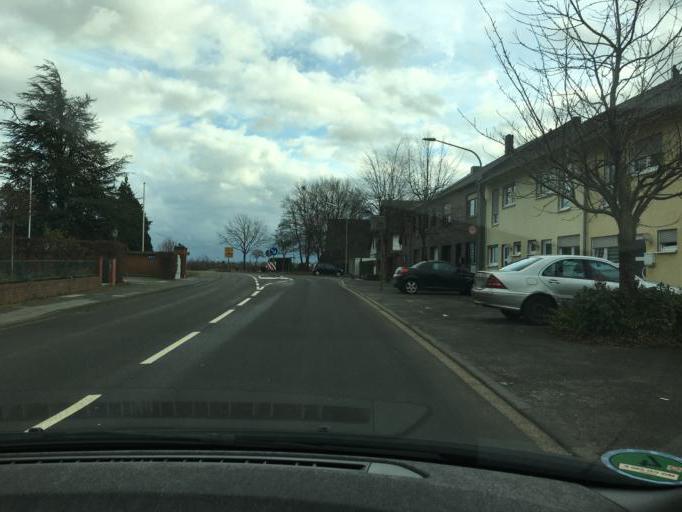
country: DE
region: North Rhine-Westphalia
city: Zulpich
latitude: 50.6698
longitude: 6.7185
